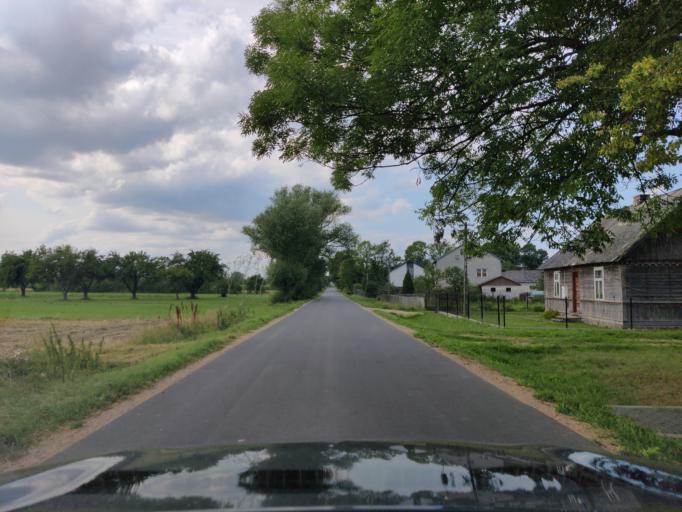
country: PL
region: Masovian Voivodeship
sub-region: Powiat pultuski
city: Obryte
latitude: 52.6885
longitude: 21.2396
